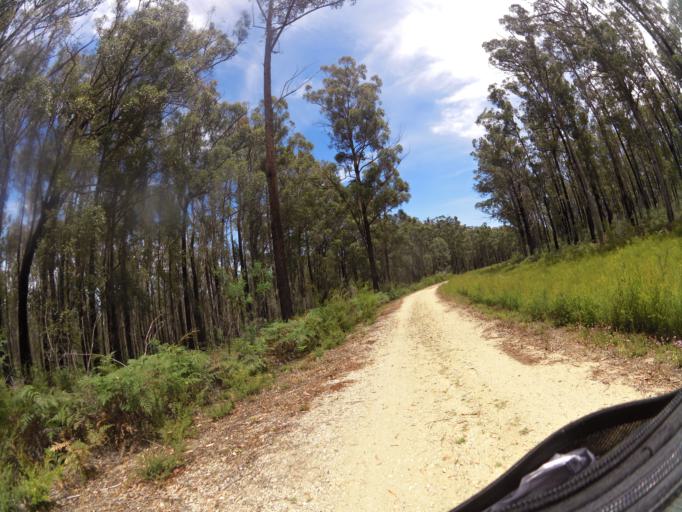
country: AU
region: Victoria
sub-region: East Gippsland
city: Lakes Entrance
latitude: -37.7450
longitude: 148.0375
